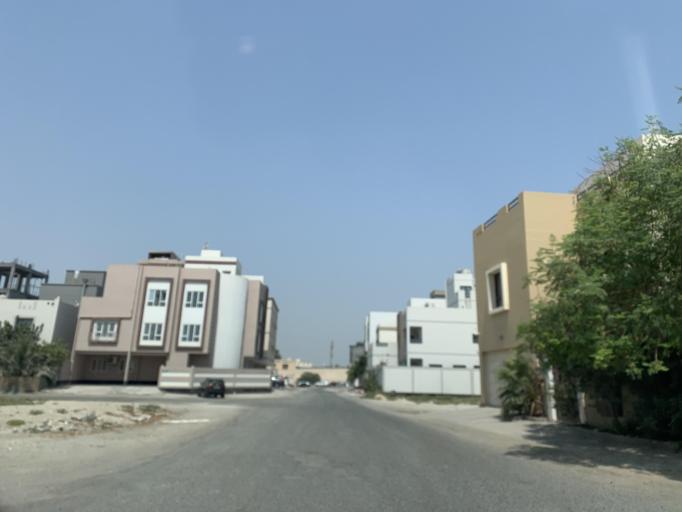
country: BH
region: Manama
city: Jidd Hafs
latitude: 26.2169
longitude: 50.5237
